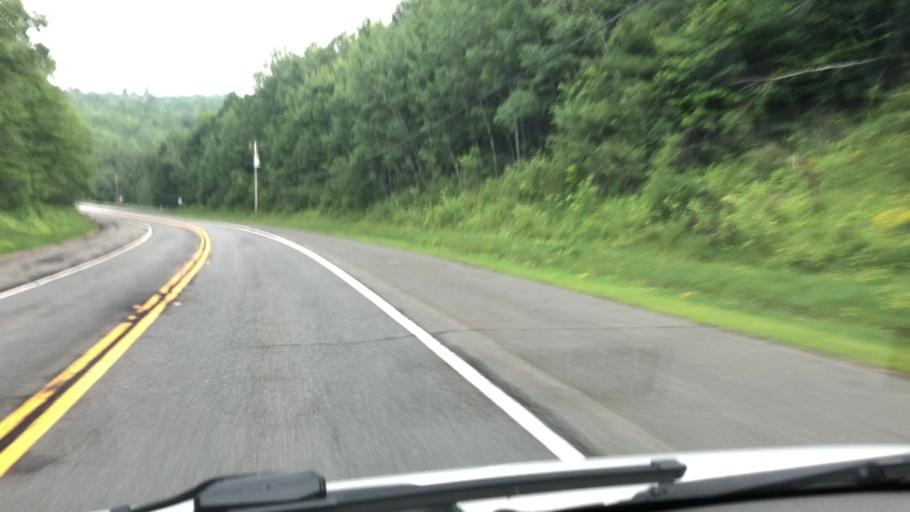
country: US
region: Massachusetts
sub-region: Berkshire County
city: Hinsdale
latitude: 42.4962
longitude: -73.0065
